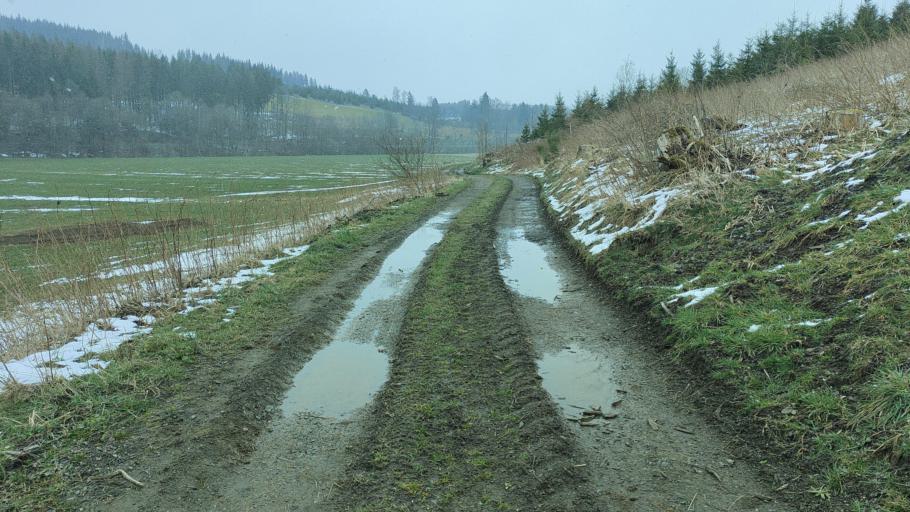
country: DE
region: North Rhine-Westphalia
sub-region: Regierungsbezirk Arnsberg
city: Bad Berleburg
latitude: 51.0902
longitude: 8.4286
